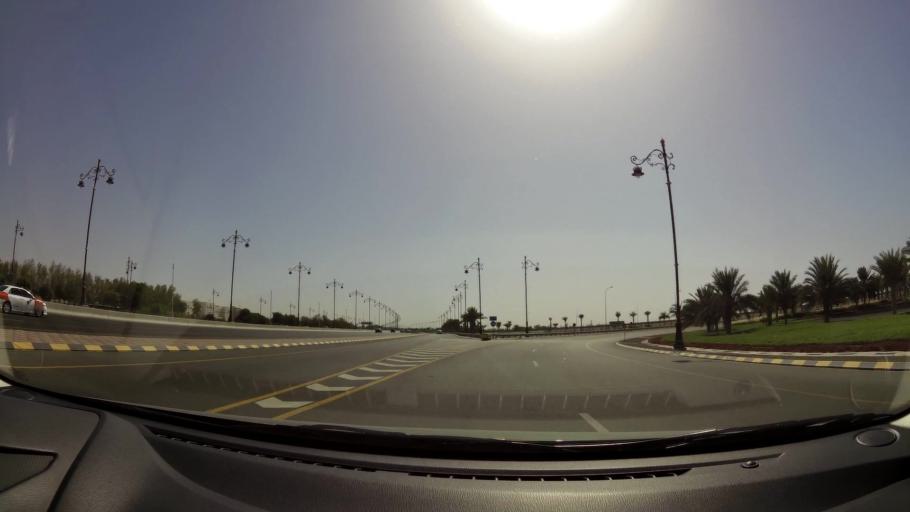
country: OM
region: Muhafazat Masqat
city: Bawshar
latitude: 23.5930
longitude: 58.3307
